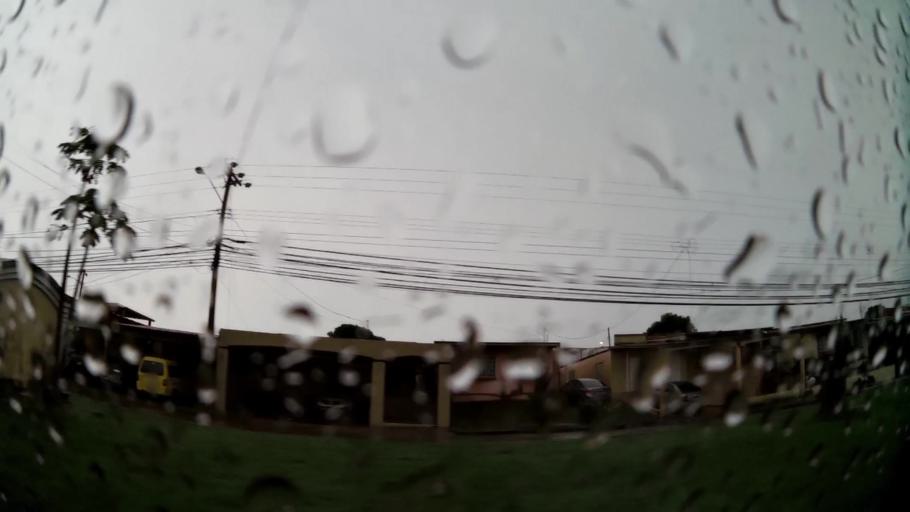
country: PA
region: Panama
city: San Miguelito
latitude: 9.0573
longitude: -79.4738
